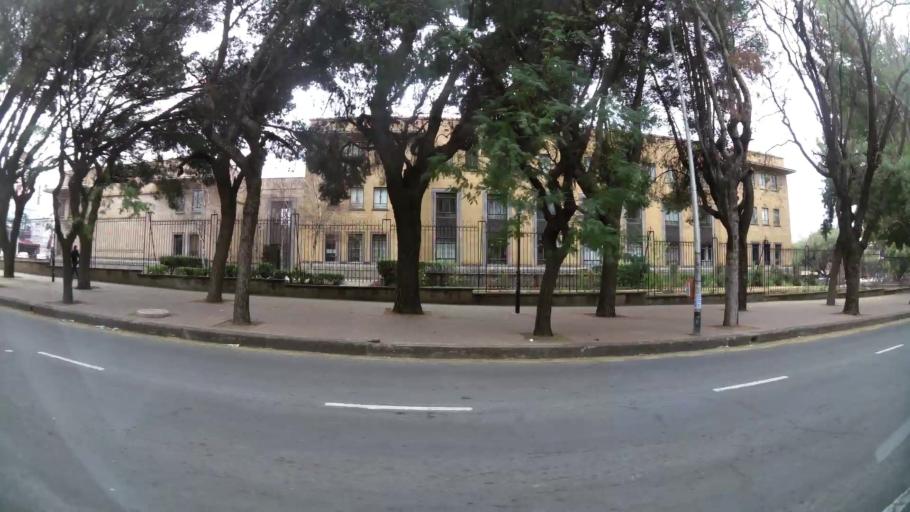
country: ZA
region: Orange Free State
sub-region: Mangaung Metropolitan Municipality
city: Bloemfontein
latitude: -29.1139
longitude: 26.2175
